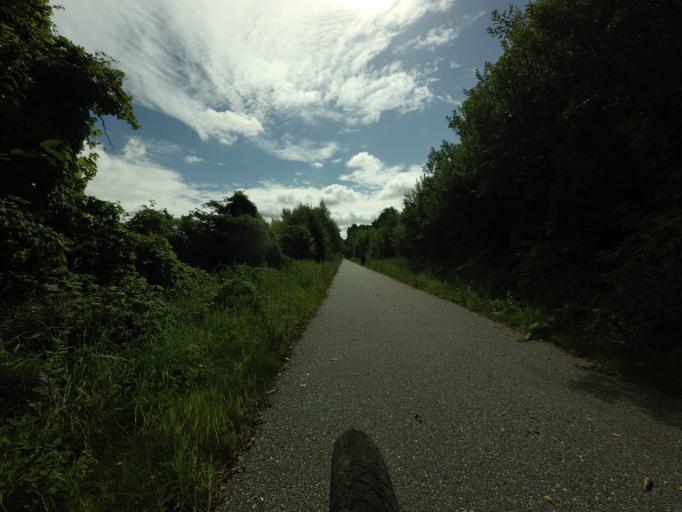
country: DK
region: Central Jutland
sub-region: Norddjurs Kommune
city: Auning
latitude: 56.4489
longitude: 10.3608
